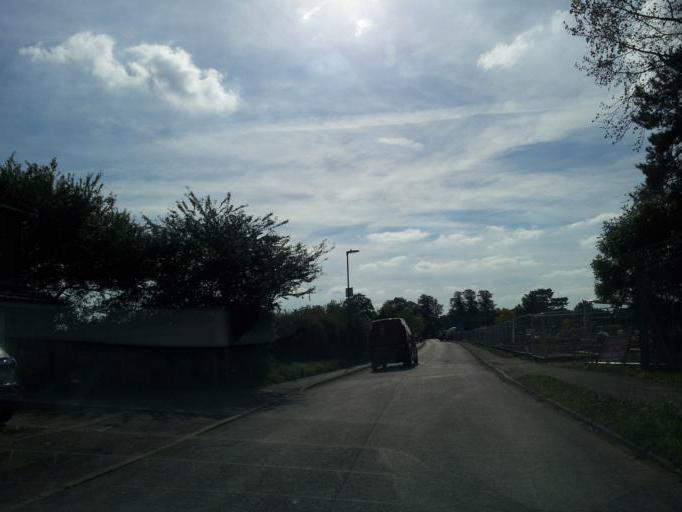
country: GB
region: England
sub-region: Cambridgeshire
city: Waterbeach
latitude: 52.2728
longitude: 0.1955
